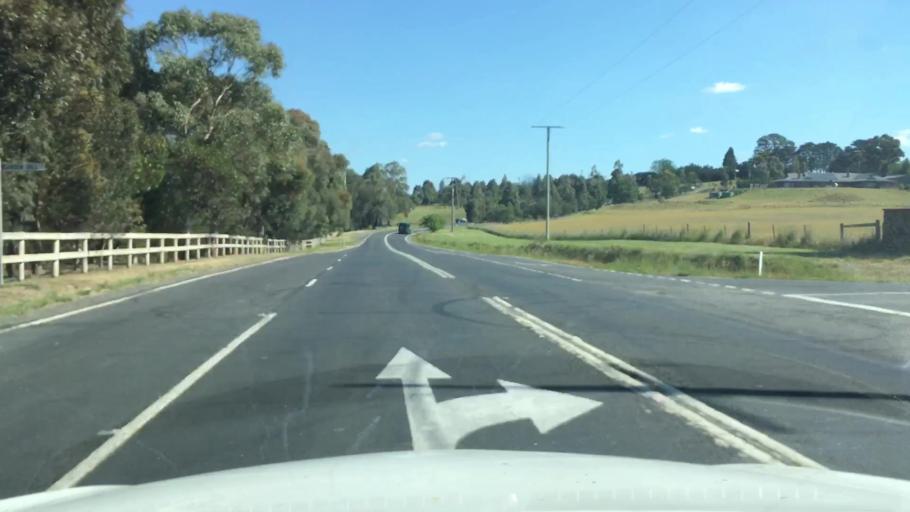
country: AU
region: Victoria
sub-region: Nillumbik
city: North Warrandyte
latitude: -37.6863
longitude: 145.2350
